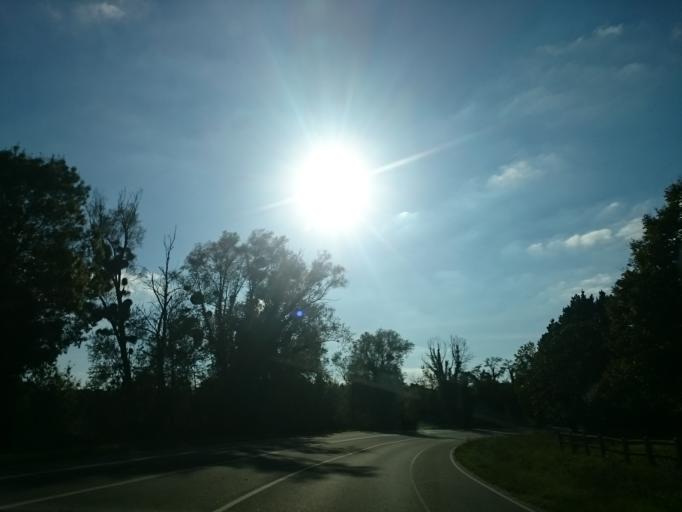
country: FR
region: Pays de la Loire
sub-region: Departement de la Loire-Atlantique
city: La Montagne
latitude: 47.1943
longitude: -1.6762
